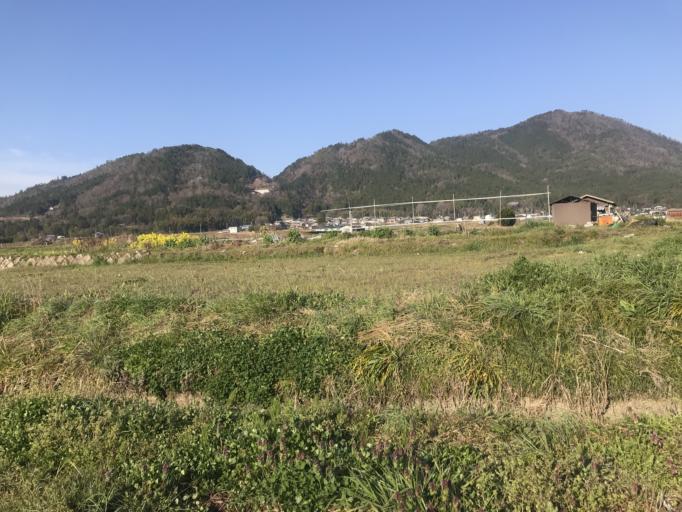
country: JP
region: Kyoto
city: Kameoka
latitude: 34.9904
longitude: 135.5435
